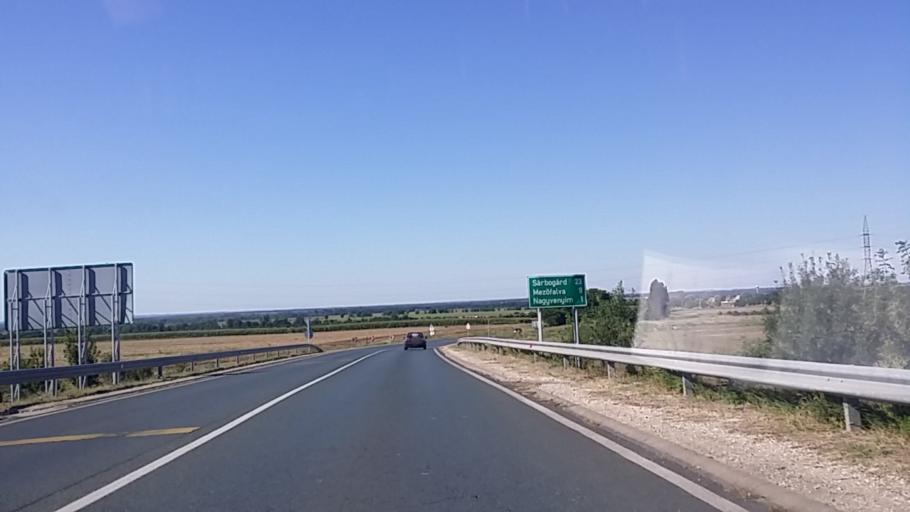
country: HU
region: Fejer
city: dunaujvaros
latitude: 46.9662
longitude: 18.8879
